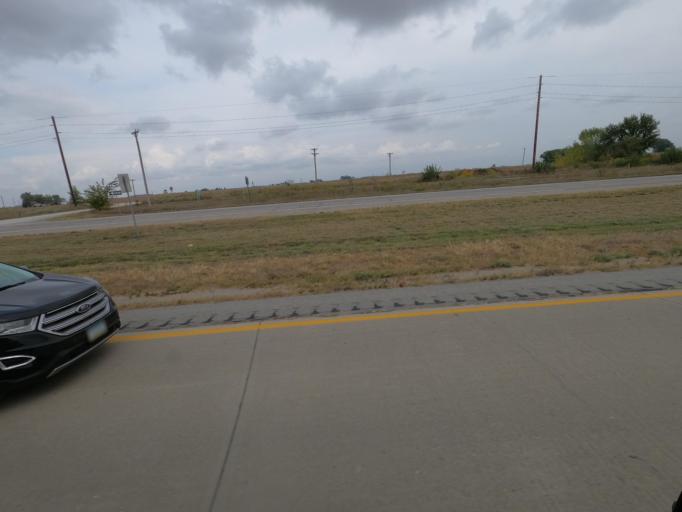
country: US
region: Iowa
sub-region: Jasper County
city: Monroe
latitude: 41.5658
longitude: -93.1590
